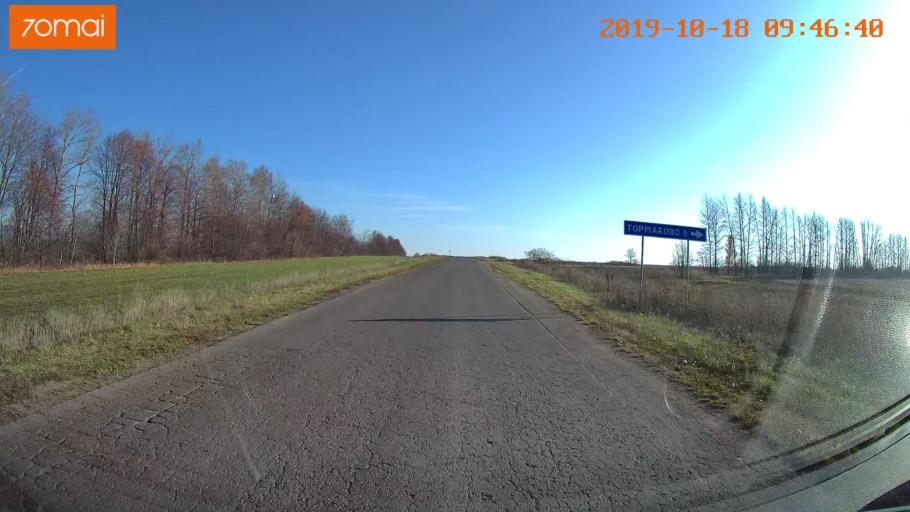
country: RU
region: Tula
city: Kazachka
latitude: 53.3130
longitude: 38.2168
